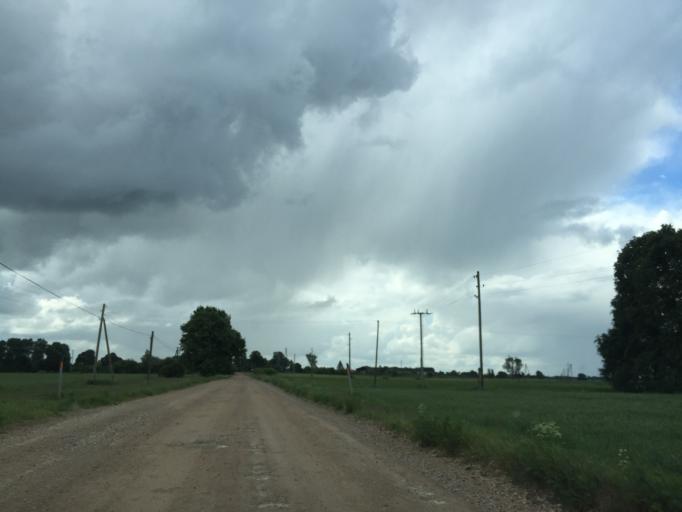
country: LV
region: Lecava
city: Iecava
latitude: 56.6121
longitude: 24.1781
